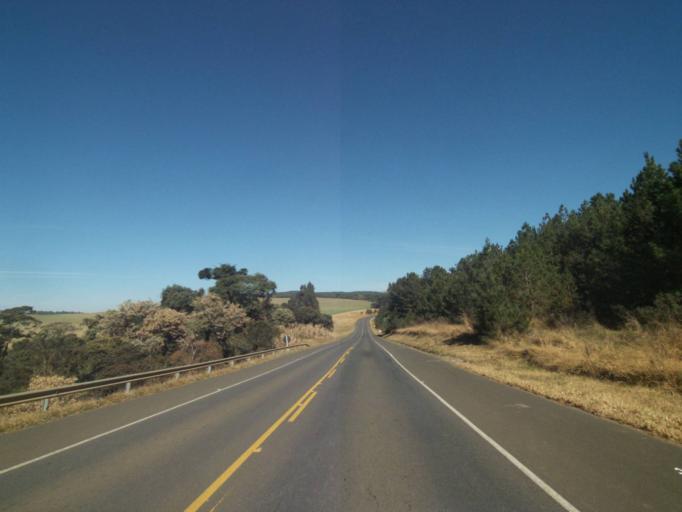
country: BR
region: Parana
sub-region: Tibagi
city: Tibagi
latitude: -24.5459
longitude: -50.4507
